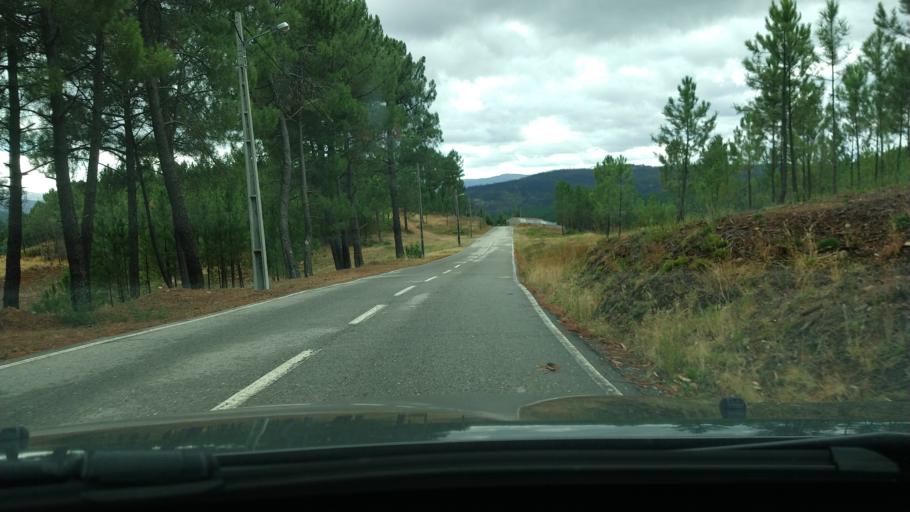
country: PT
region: Castelo Branco
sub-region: Covilha
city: Covilha
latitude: 40.2335
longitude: -7.6481
